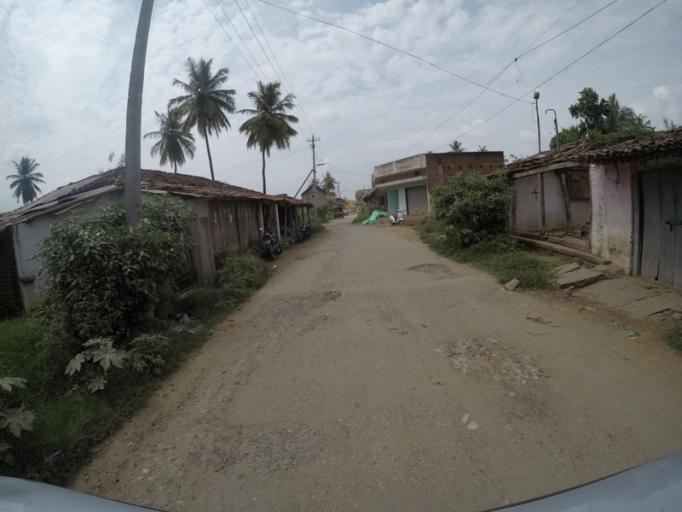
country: IN
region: Karnataka
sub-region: Mandya
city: Malavalli
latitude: 12.4234
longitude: 77.2253
